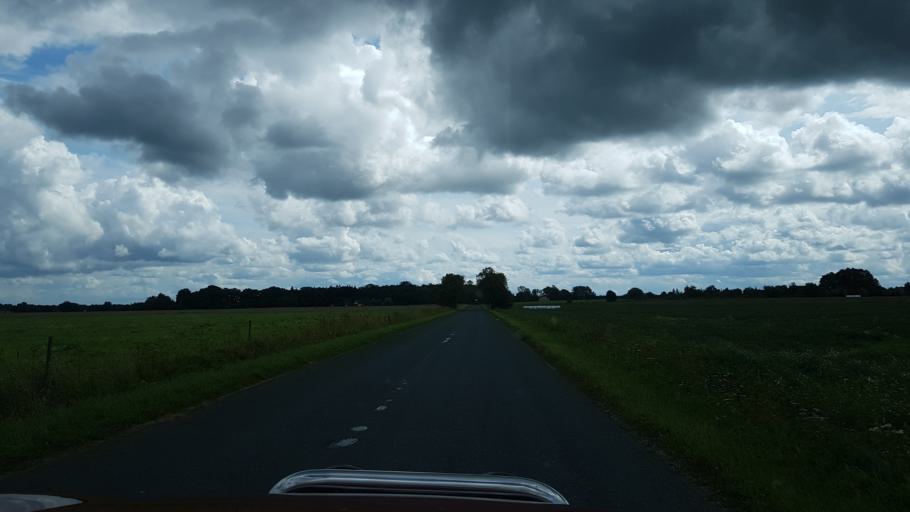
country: EE
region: Laeaene
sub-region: Lihula vald
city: Lihula
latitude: 58.7108
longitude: 24.0117
